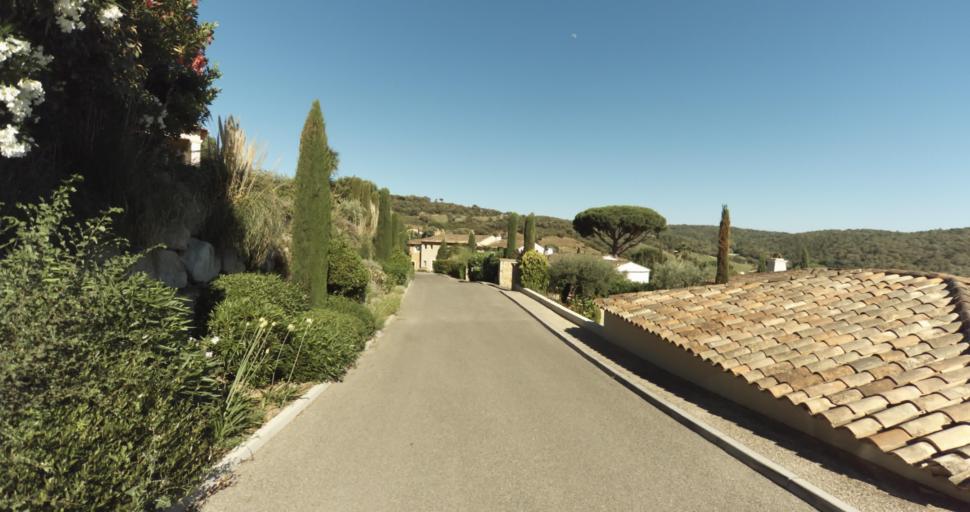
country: FR
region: Provence-Alpes-Cote d'Azur
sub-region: Departement du Var
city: Gassin
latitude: 43.2557
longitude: 6.6035
